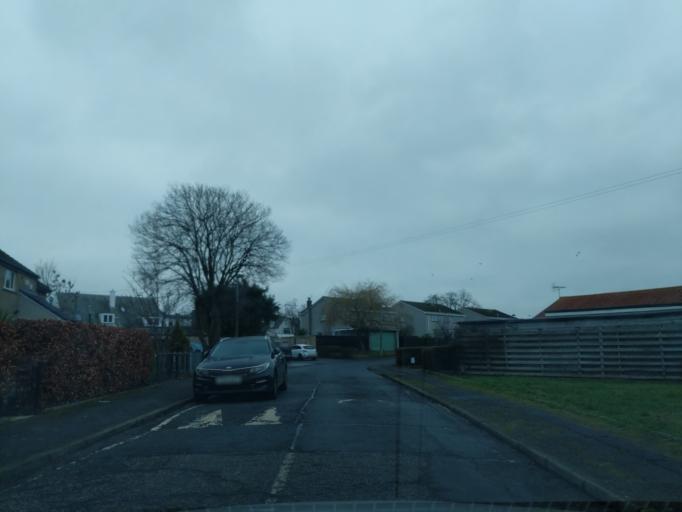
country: GB
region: Scotland
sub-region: Edinburgh
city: Currie
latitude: 55.8926
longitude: -3.3243
